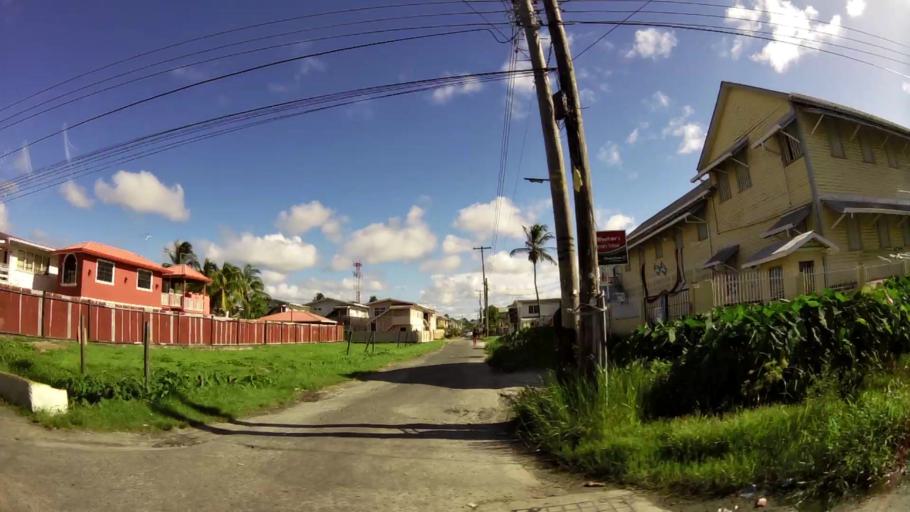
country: GY
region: Demerara-Mahaica
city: Georgetown
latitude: 6.8135
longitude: -58.1423
